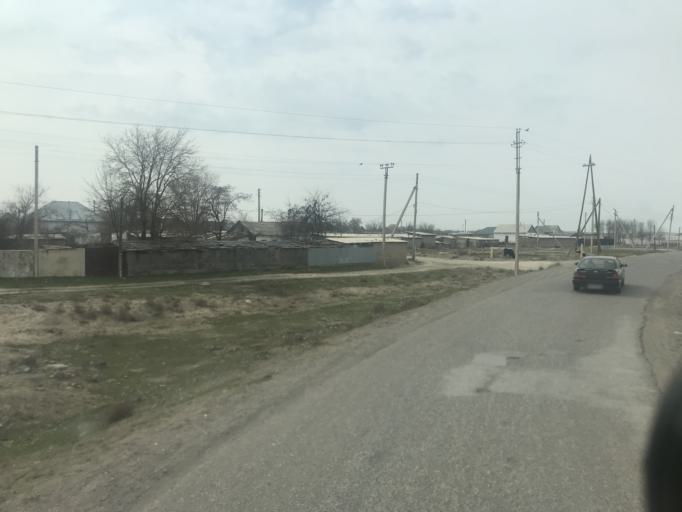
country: KZ
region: Ongtustik Qazaqstan
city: Shardara
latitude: 41.2641
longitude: 67.9484
